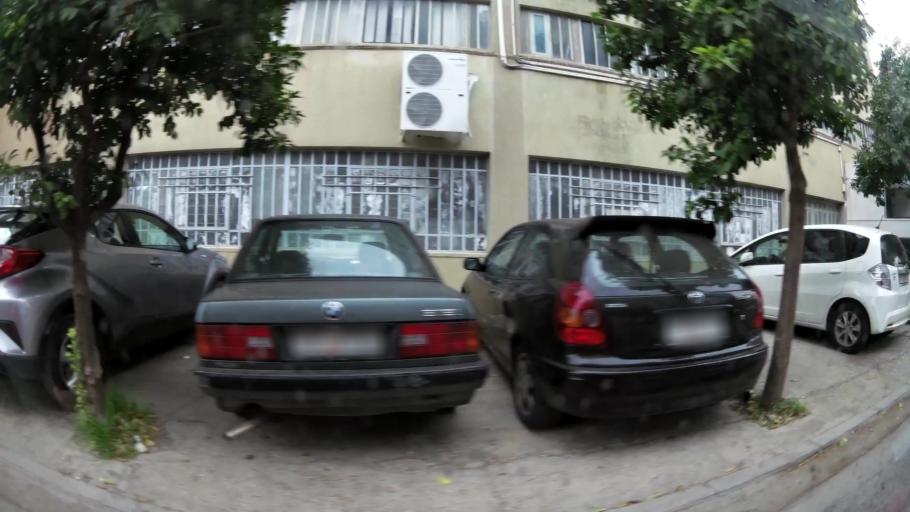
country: GR
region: Attica
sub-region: Nomarchia Athinas
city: Peristeri
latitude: 38.0083
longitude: 23.7103
